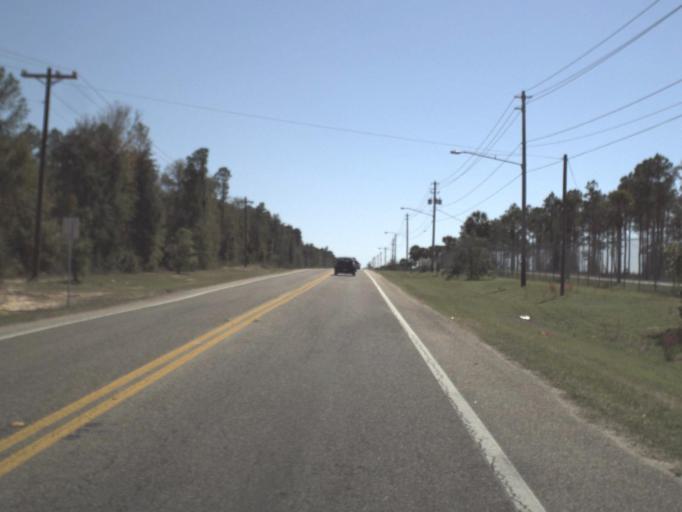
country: US
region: Florida
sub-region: Leon County
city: Tallahassee
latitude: 30.4146
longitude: -84.3530
